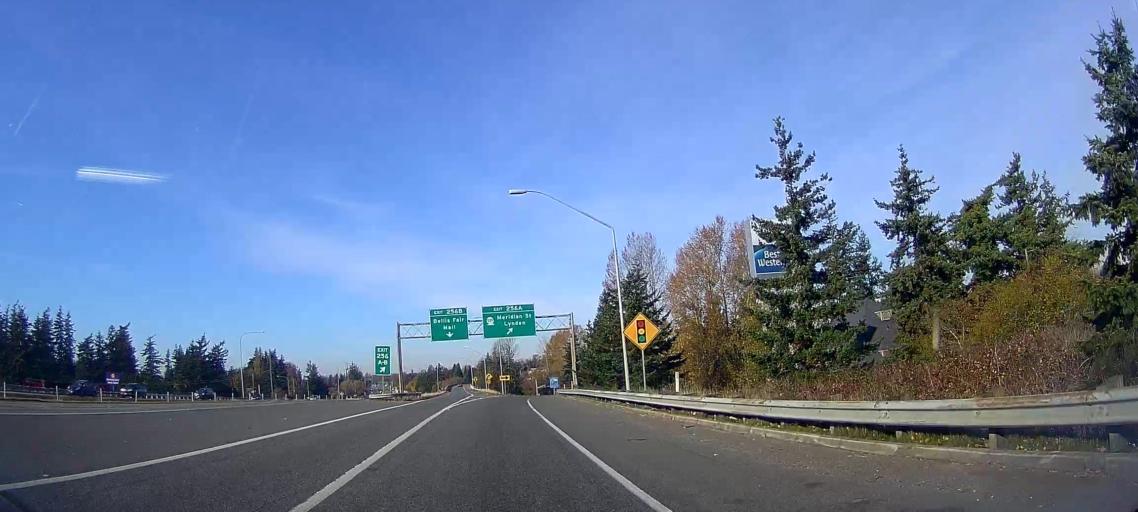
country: US
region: Washington
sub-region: Whatcom County
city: Bellingham
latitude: 48.7827
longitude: -122.4834
